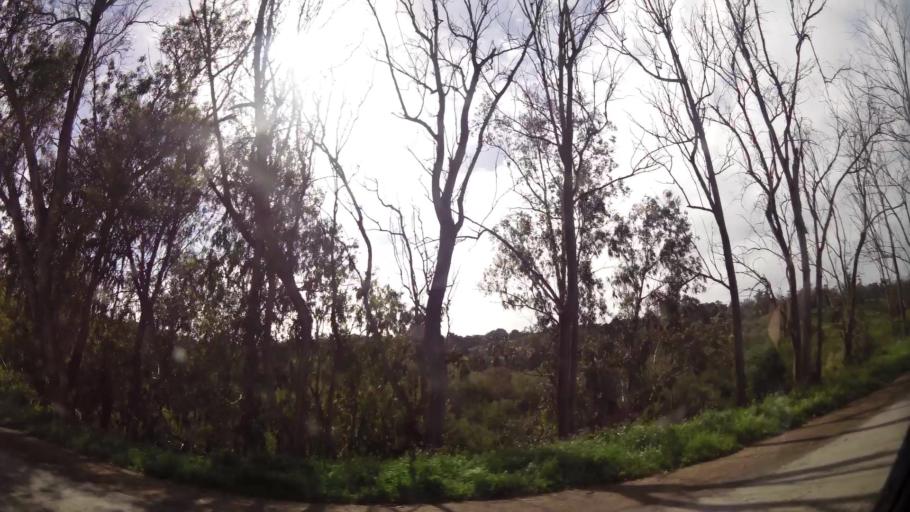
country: MA
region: Grand Casablanca
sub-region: Mohammedia
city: Mohammedia
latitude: 33.6605
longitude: -7.3991
